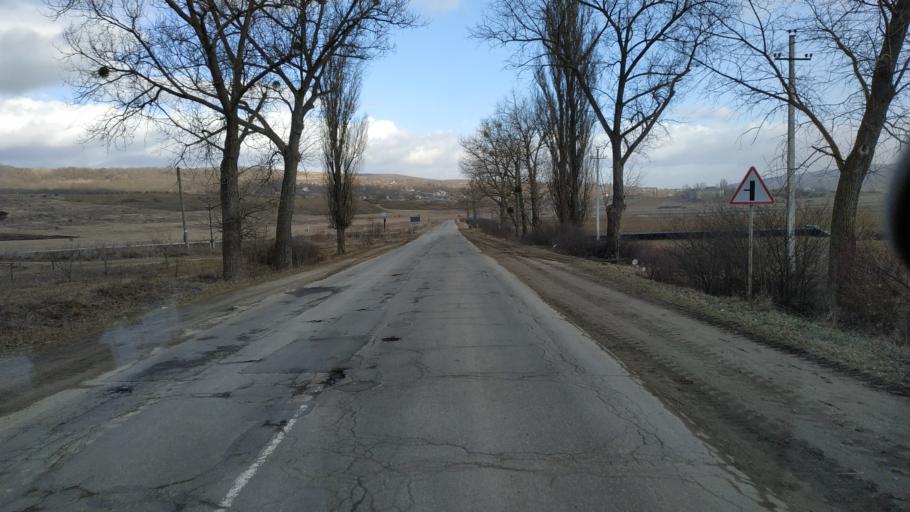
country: MD
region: Calarasi
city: Calarasi
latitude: 47.3284
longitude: 28.0940
